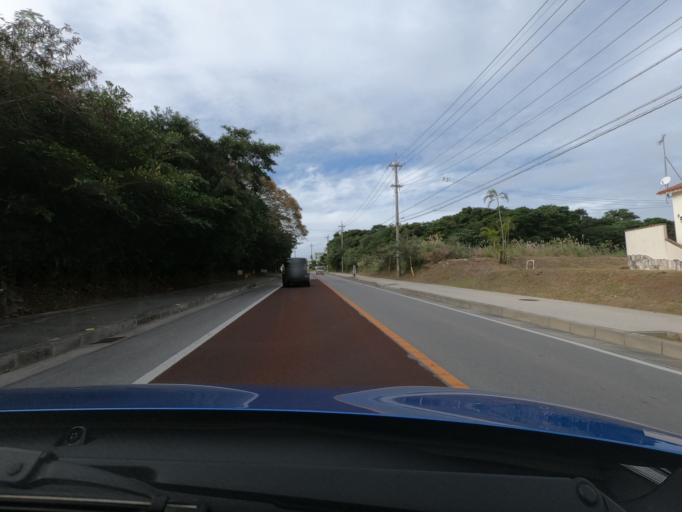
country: JP
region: Okinawa
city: Nago
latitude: 26.6796
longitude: 127.8872
